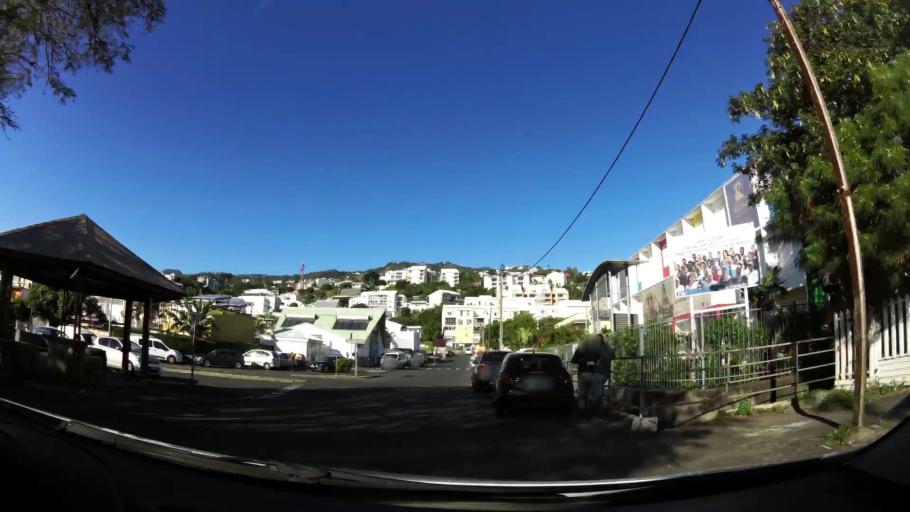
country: RE
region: Reunion
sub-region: Reunion
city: Saint-Denis
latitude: -20.8903
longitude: 55.4481
